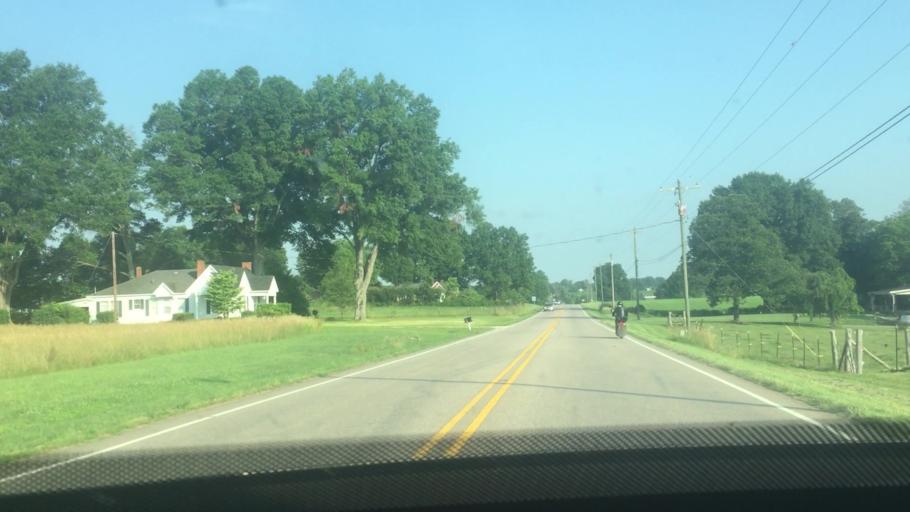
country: US
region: North Carolina
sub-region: Iredell County
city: Mooresville
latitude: 35.5878
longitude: -80.7477
